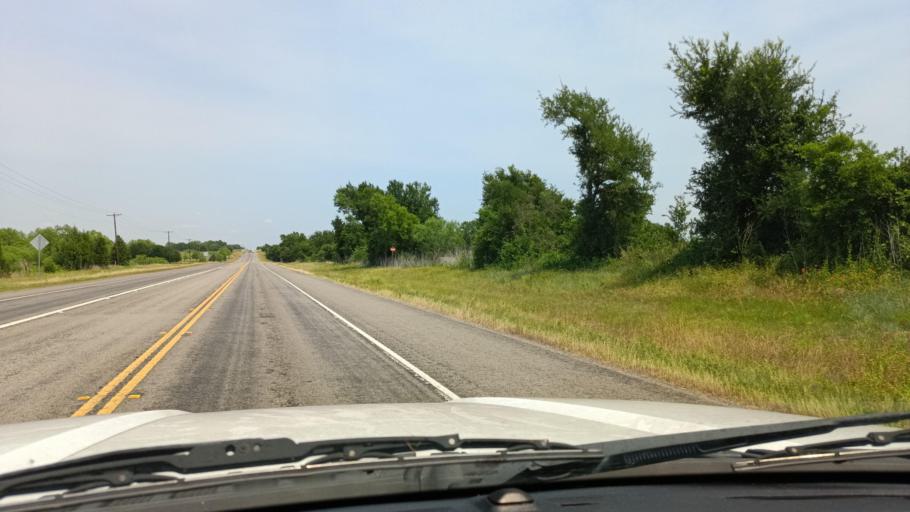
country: US
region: Texas
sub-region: Milam County
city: Cameron
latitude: 30.8488
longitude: -97.0679
